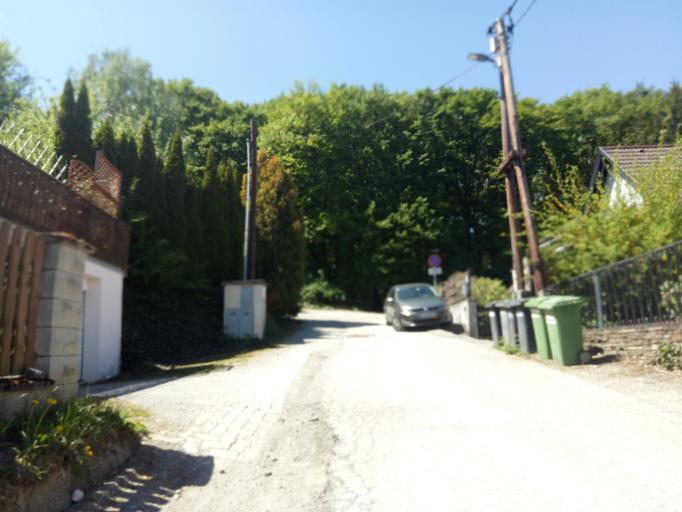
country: AT
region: Lower Austria
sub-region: Politischer Bezirk Modling
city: Kaltenleutgeben
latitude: 48.1263
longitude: 16.1792
